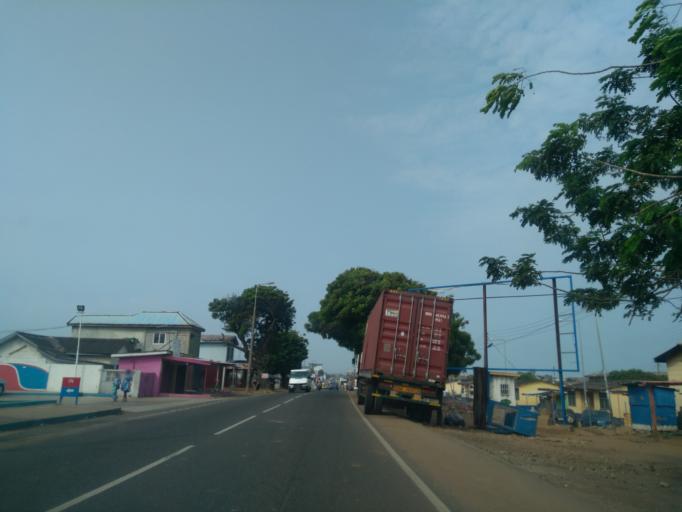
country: GH
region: Greater Accra
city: Accra
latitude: 5.5519
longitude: -0.1791
